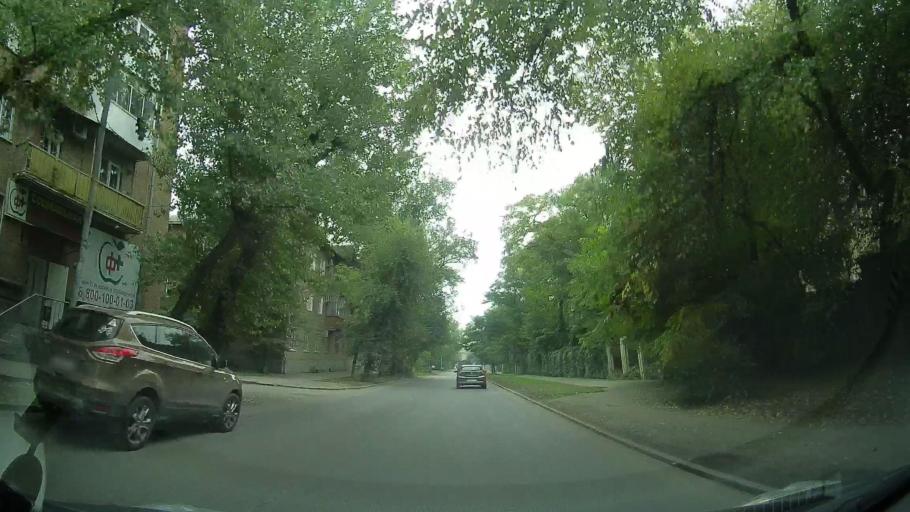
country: RU
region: Rostov
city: Rostov-na-Donu
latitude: 47.2537
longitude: 39.7055
